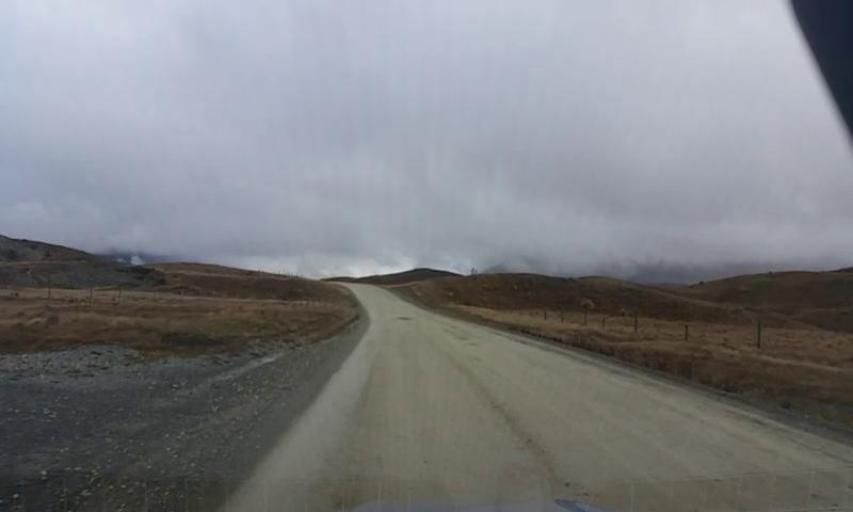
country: NZ
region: Canterbury
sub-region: Ashburton District
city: Methven
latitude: -43.6149
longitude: 171.1416
